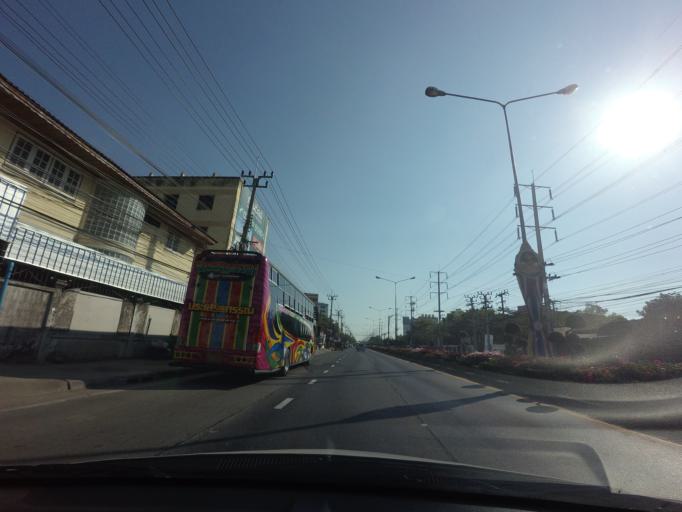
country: TH
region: Bangkok
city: Nong Chok
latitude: 13.8464
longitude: 100.8582
